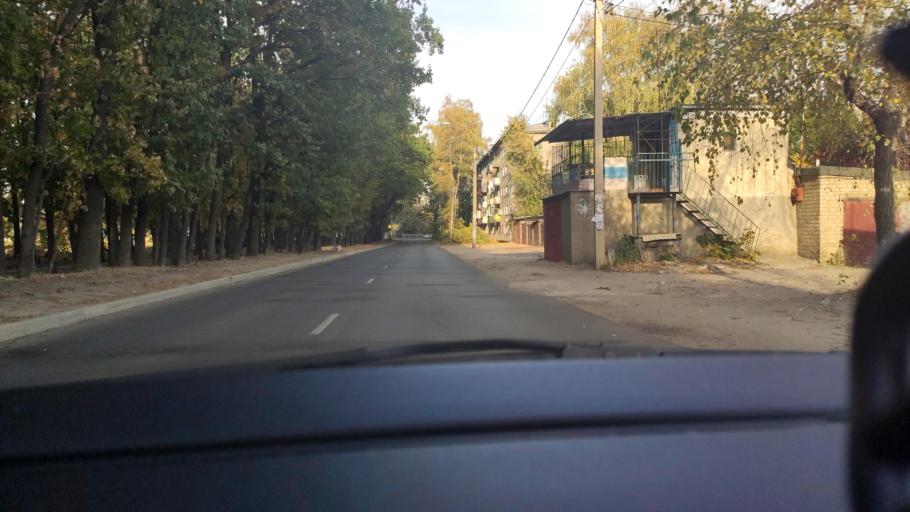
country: RU
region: Voronezj
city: Voronezh
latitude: 51.7031
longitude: 39.2271
